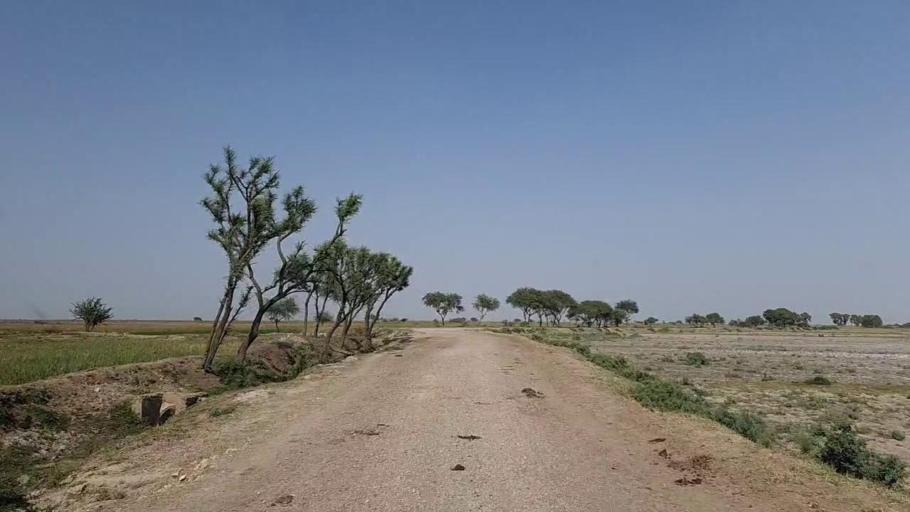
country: PK
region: Sindh
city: Jati
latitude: 24.3486
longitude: 68.3089
